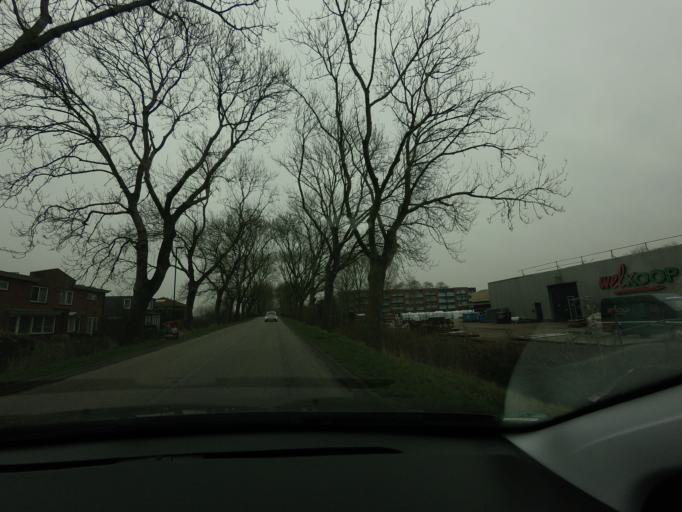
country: NL
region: Friesland
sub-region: Sudwest Fryslan
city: Bolsward
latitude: 53.0643
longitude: 5.5116
